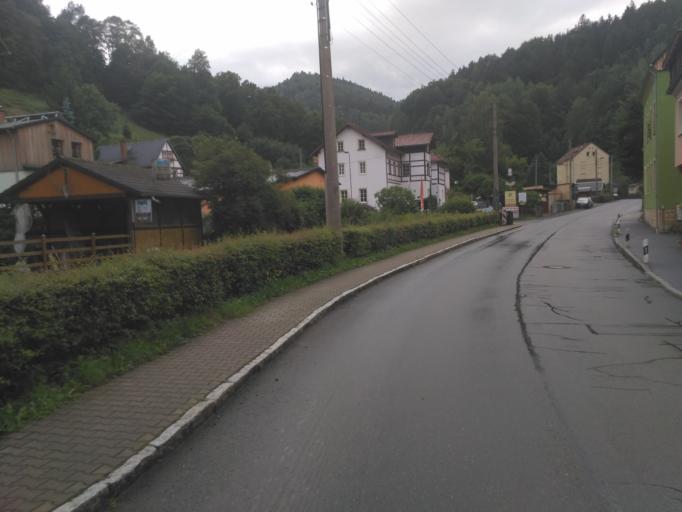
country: DE
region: Saxony
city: Bad Schandau
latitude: 50.9065
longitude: 14.1663
